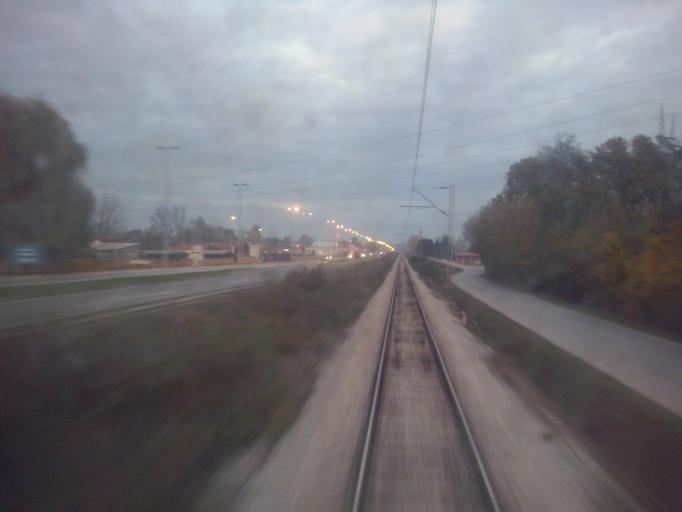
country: RS
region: Central Serbia
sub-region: Kolubarski Okrug
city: Valjevo
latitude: 44.2826
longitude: 19.9320
